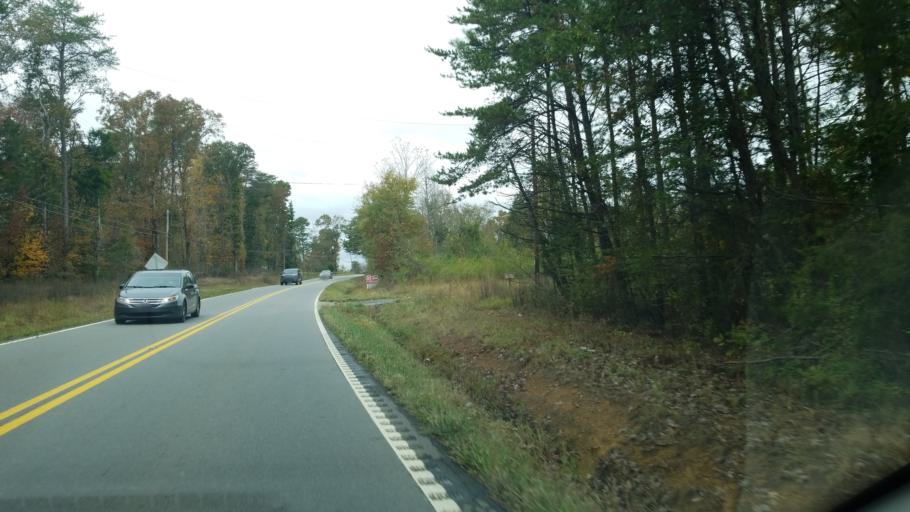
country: US
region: Tennessee
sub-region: Hamilton County
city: Sale Creek
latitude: 35.3679
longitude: -84.9918
